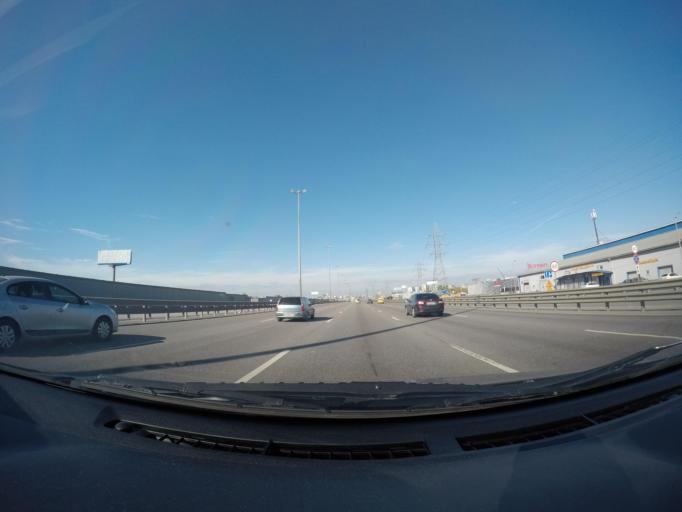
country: RU
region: Moskovskaya
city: Lyubertsy
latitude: 55.6499
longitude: 37.9080
